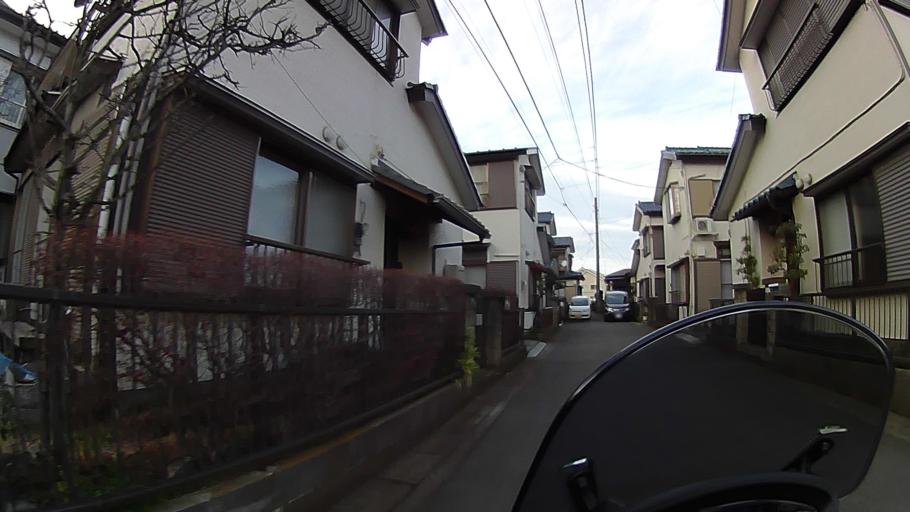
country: JP
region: Kanagawa
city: Atsugi
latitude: 35.4274
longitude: 139.4198
